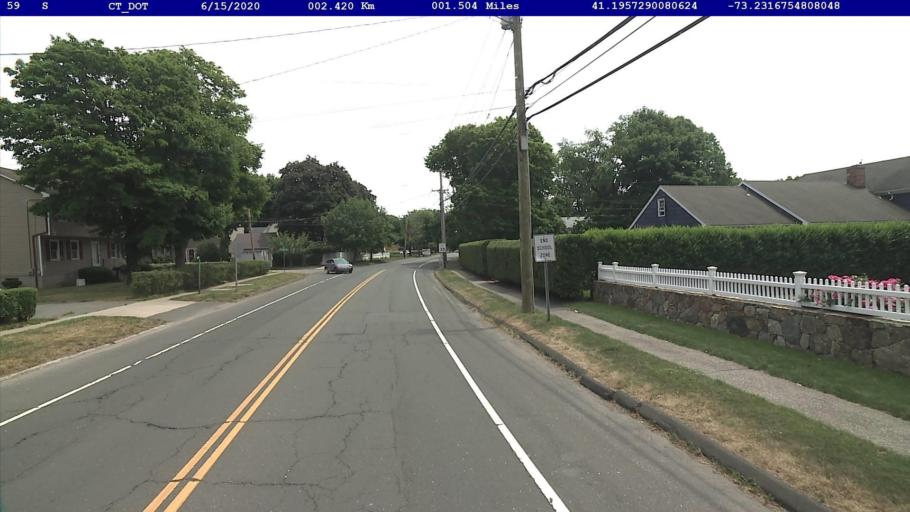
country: US
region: Connecticut
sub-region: Fairfield County
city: Bridgeport
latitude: 41.1957
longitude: -73.2317
